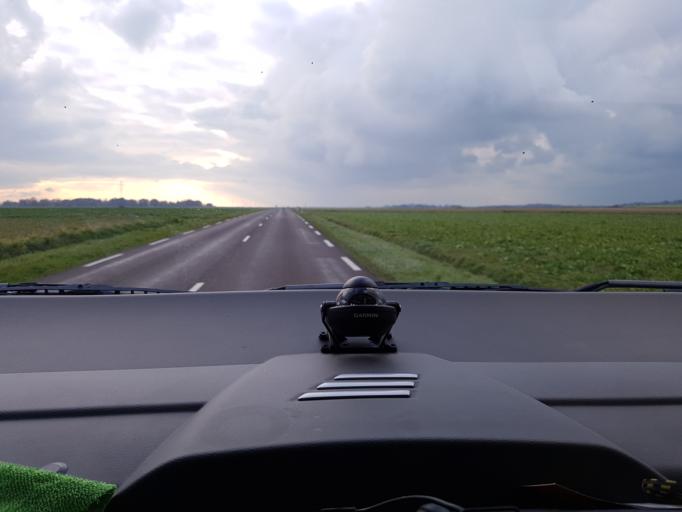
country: FR
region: Haute-Normandie
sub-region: Departement de la Seine-Maritime
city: Hautot-sur-Mer
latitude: 49.8901
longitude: 1.0260
